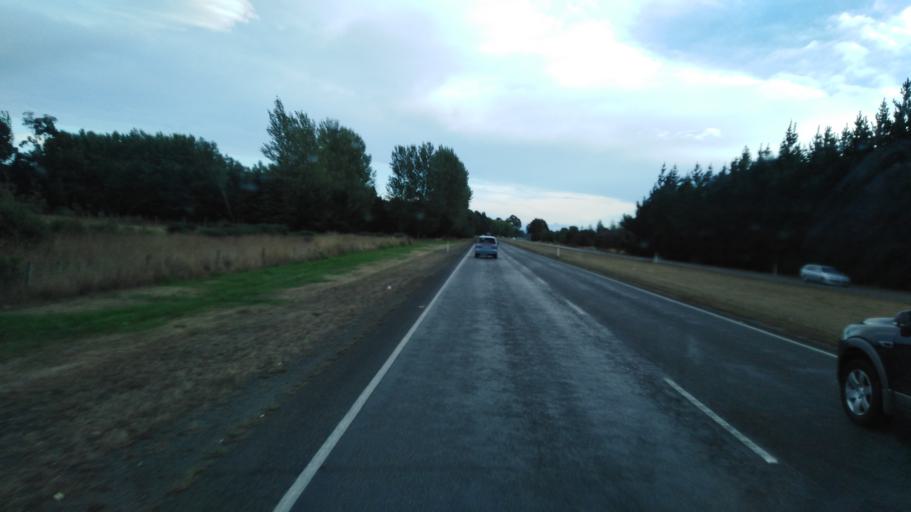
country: NZ
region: Canterbury
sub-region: Waimakariri District
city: Kaiapoi
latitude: -43.3975
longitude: 172.6413
